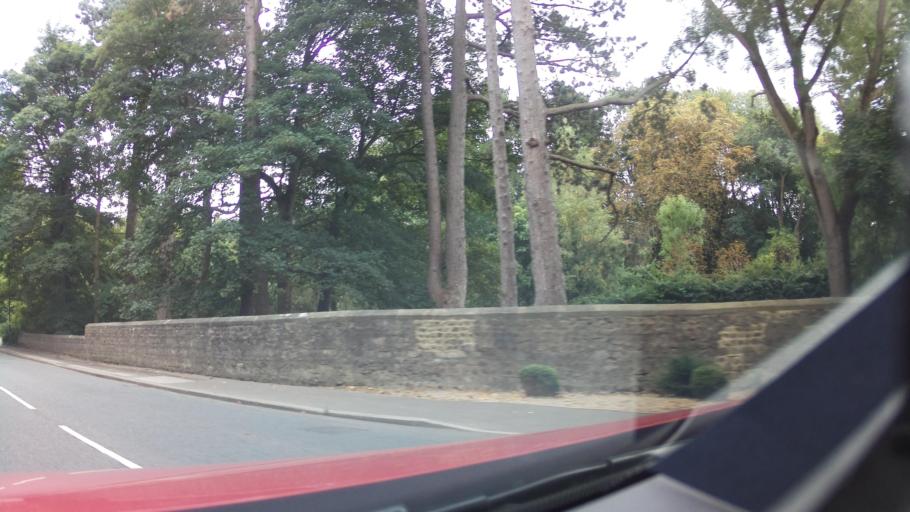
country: GB
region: England
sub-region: North Yorkshire
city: Ripon
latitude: 54.1444
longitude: -1.5276
